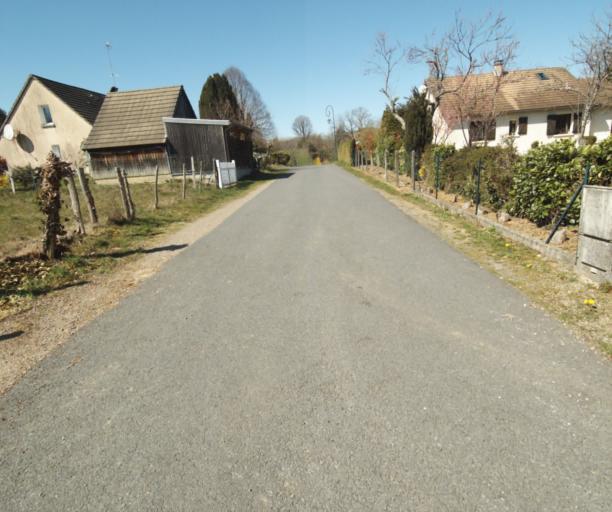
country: FR
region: Limousin
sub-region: Departement de la Correze
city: Saint-Mexant
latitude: 45.2854
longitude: 1.6602
